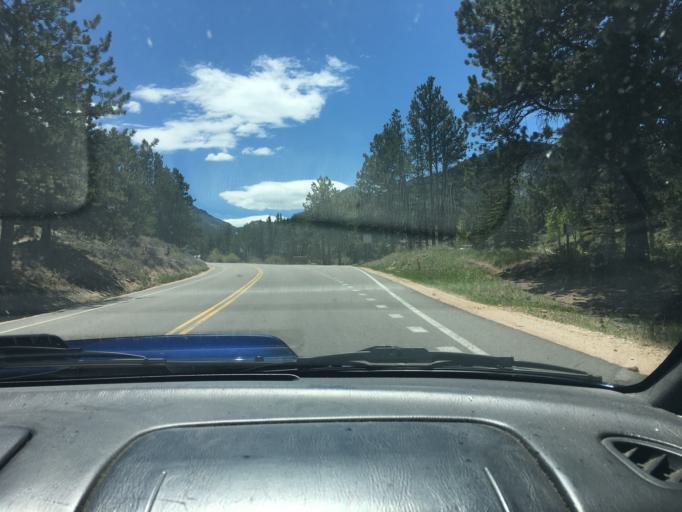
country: US
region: Colorado
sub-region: Larimer County
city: Estes Park
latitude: 40.3425
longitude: -105.5675
